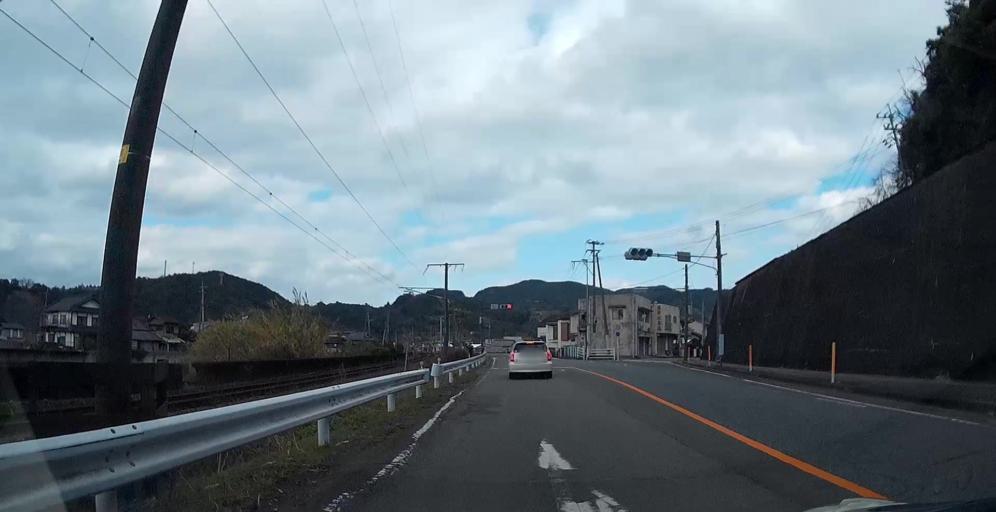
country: JP
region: Kumamoto
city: Yatsushiro
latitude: 32.3580
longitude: 130.5079
